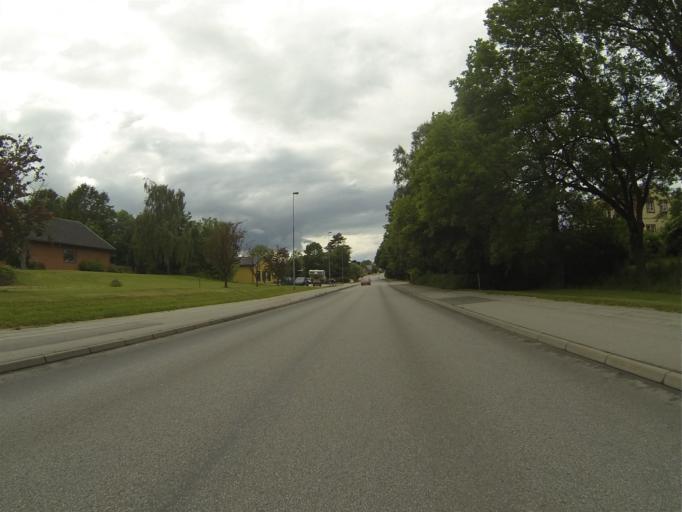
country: SE
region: Skane
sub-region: Lunds Kommun
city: Genarp
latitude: 55.6626
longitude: 13.3551
